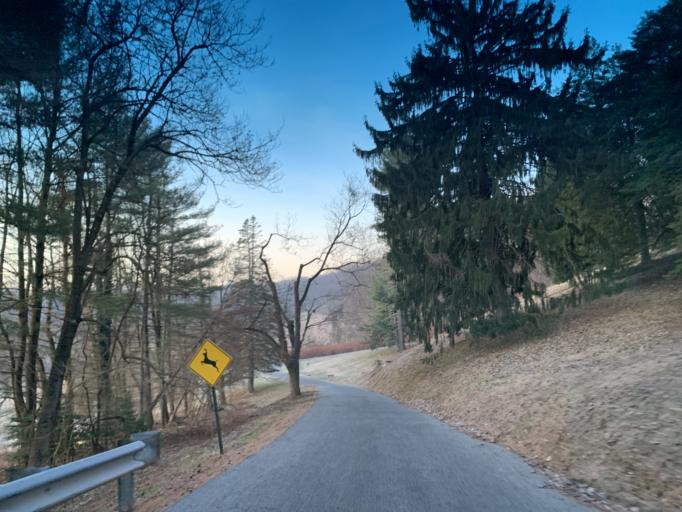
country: US
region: Maryland
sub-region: Baltimore County
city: Carney
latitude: 39.4471
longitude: -76.5167
